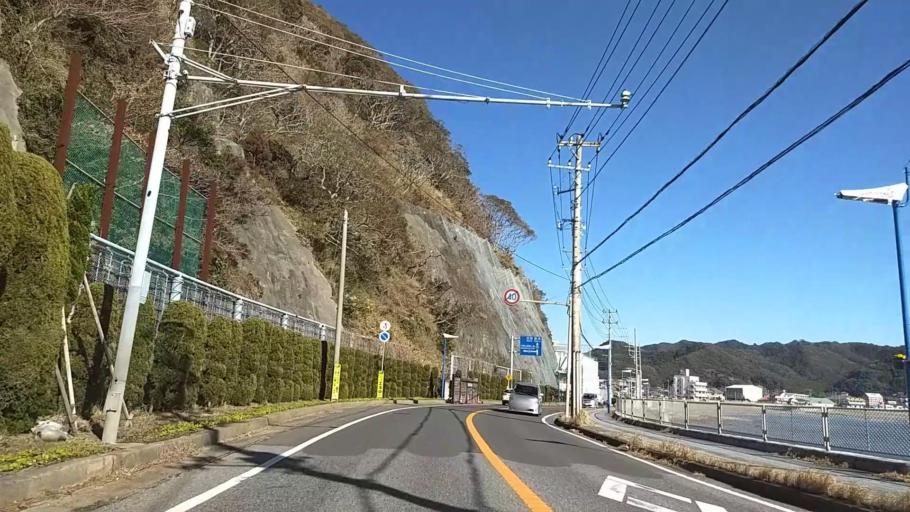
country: JP
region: Chiba
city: Kawaguchi
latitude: 35.1257
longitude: 140.1861
